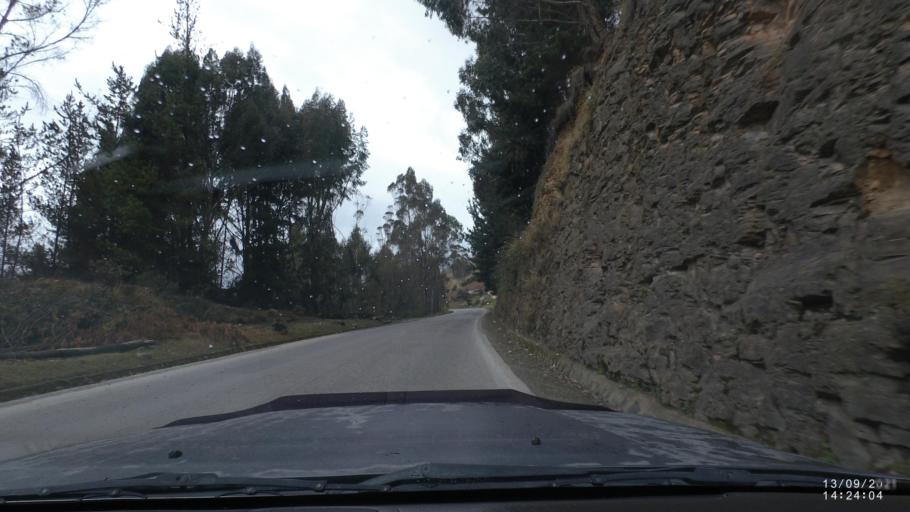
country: BO
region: Cochabamba
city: Colomi
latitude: -17.2813
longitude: -65.8739
